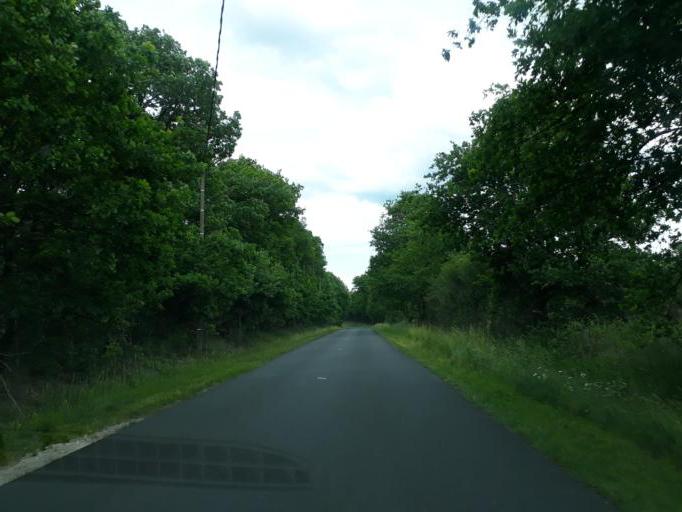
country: FR
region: Centre
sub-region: Departement du Loiret
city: La Ferte-Saint-Aubin
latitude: 47.7253
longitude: 1.9673
